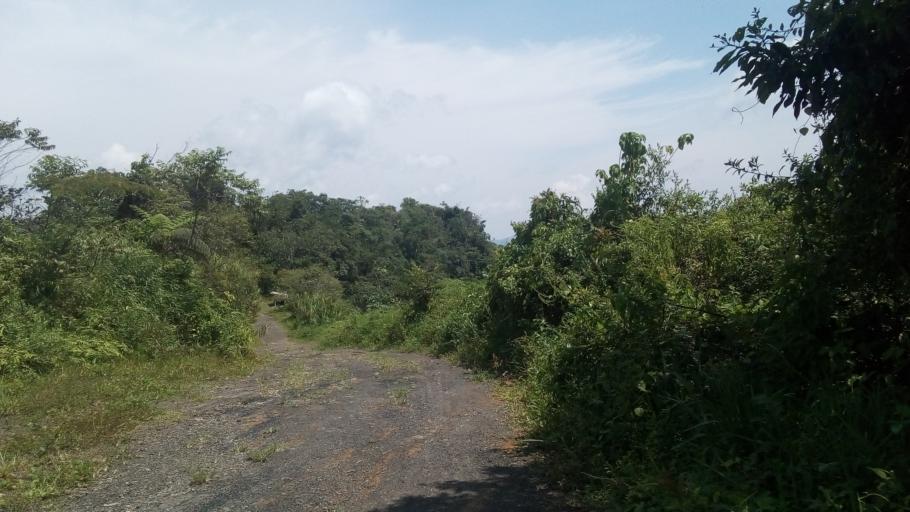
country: CO
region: Boyaca
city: Otanche
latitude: 5.6290
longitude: -74.2415
